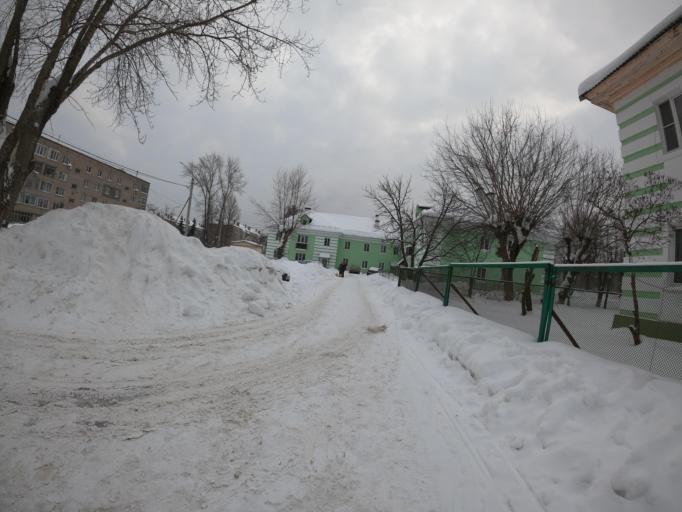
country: RU
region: Moskovskaya
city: Elektrogorsk
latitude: 55.8794
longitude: 38.7855
